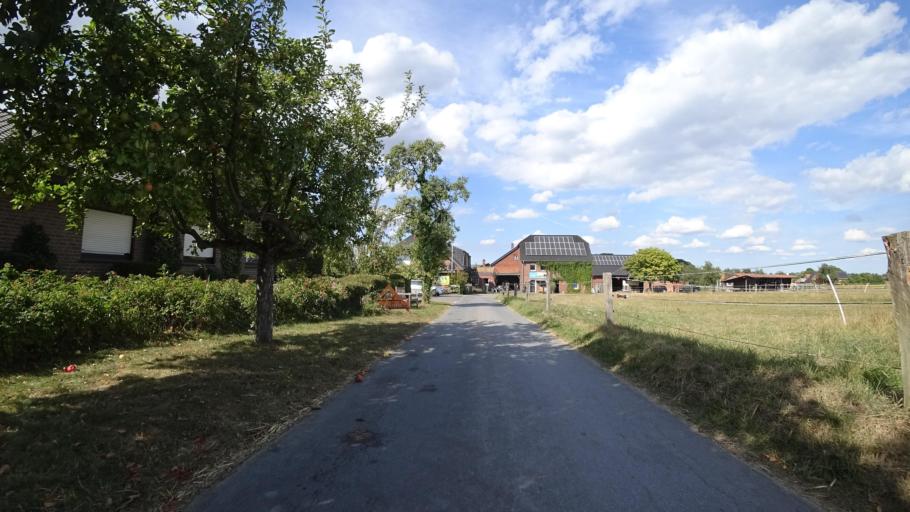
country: DE
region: North Rhine-Westphalia
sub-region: Regierungsbezirk Detmold
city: Rheda-Wiedenbruck
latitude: 51.8276
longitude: 8.2815
